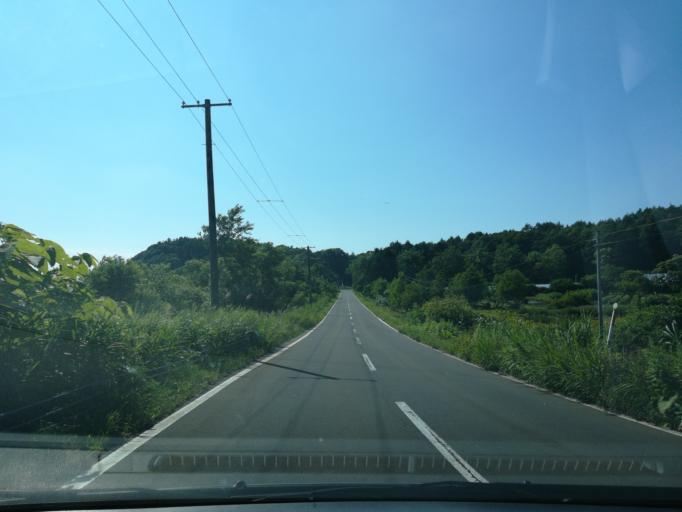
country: JP
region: Hokkaido
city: Chitose
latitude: 42.9106
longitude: 141.7307
